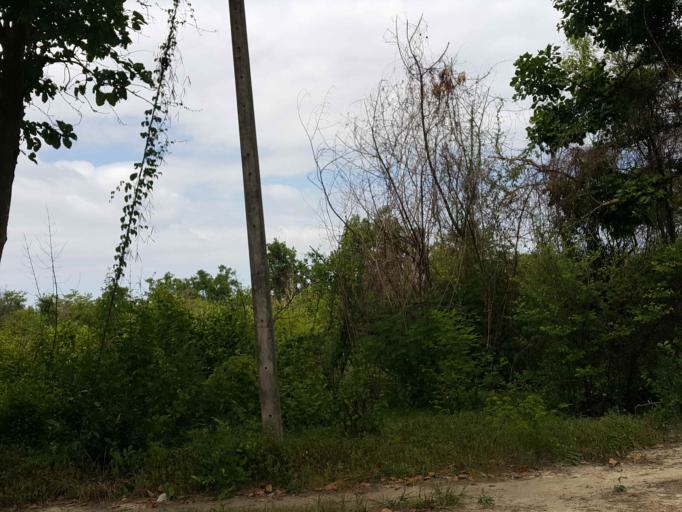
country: TH
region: Chiang Mai
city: San Kamphaeng
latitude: 18.7561
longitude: 99.0922
